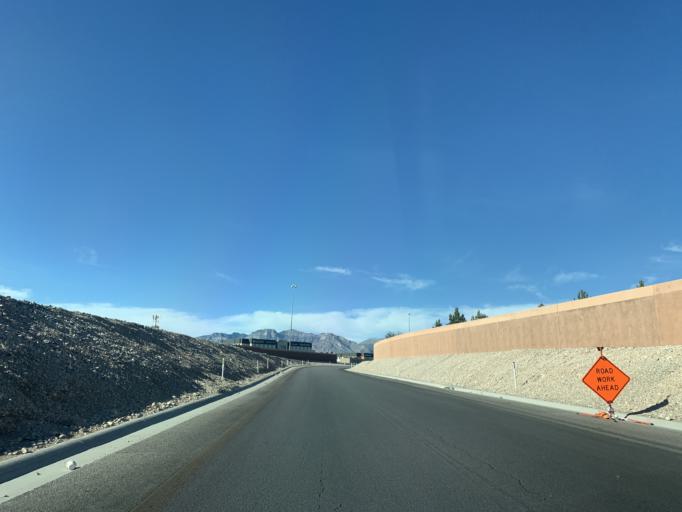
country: US
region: Nevada
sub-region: Clark County
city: Summerlin South
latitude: 36.1009
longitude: -115.2930
